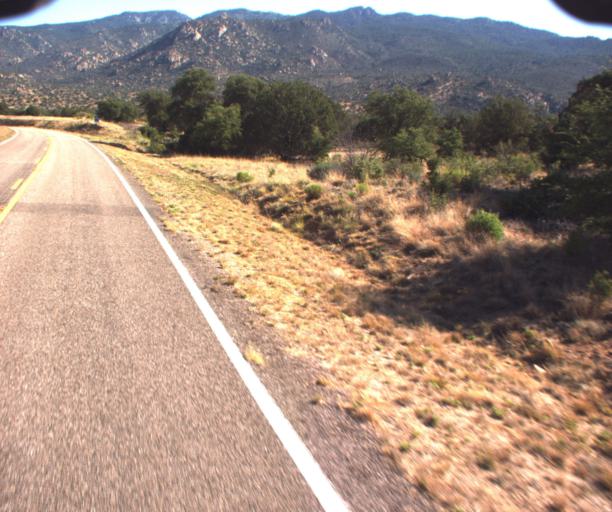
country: US
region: Arizona
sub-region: Graham County
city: Swift Trail Junction
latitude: 32.5899
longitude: -109.8545
